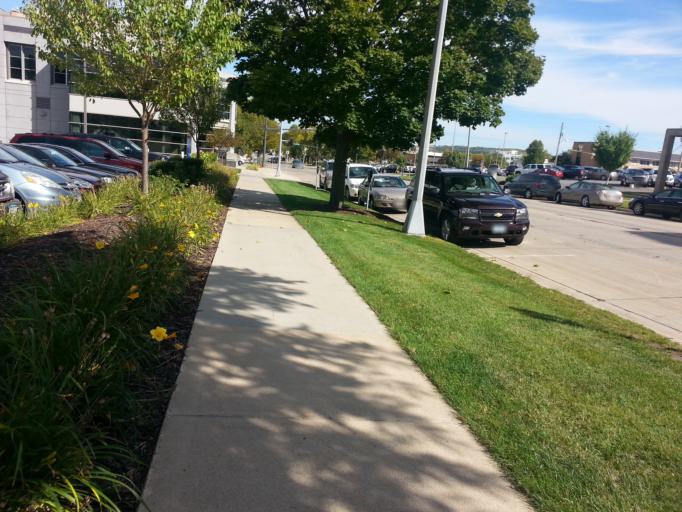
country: US
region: Minnesota
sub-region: Olmsted County
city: Rochester
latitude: 44.0195
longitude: -92.4694
